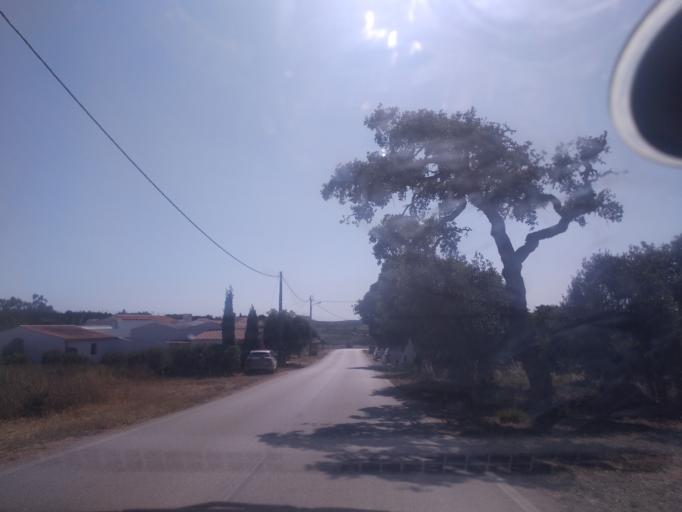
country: PT
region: Faro
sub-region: Aljezur
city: Aljezur
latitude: 37.2274
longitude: -8.8190
